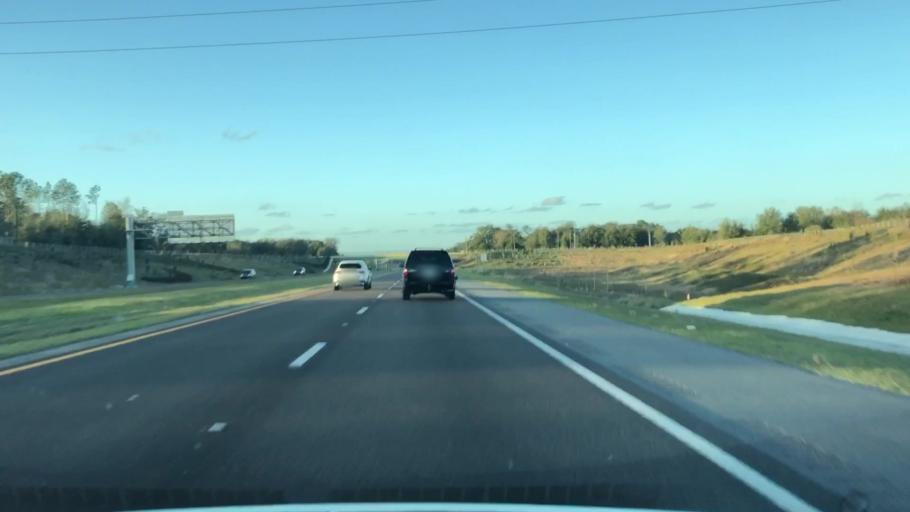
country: US
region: Florida
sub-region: Orange County
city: Zellwood
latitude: 28.7091
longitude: -81.5601
